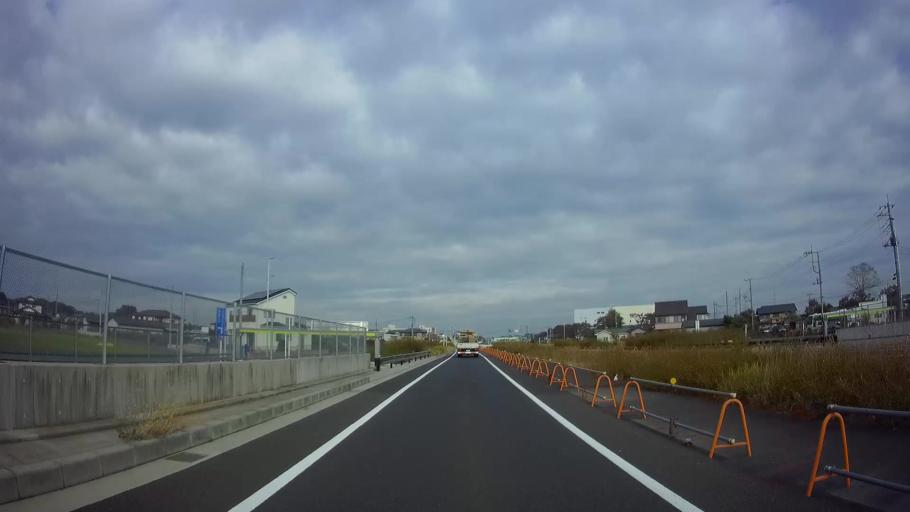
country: JP
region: Saitama
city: Okegawa
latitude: 35.9795
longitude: 139.5365
